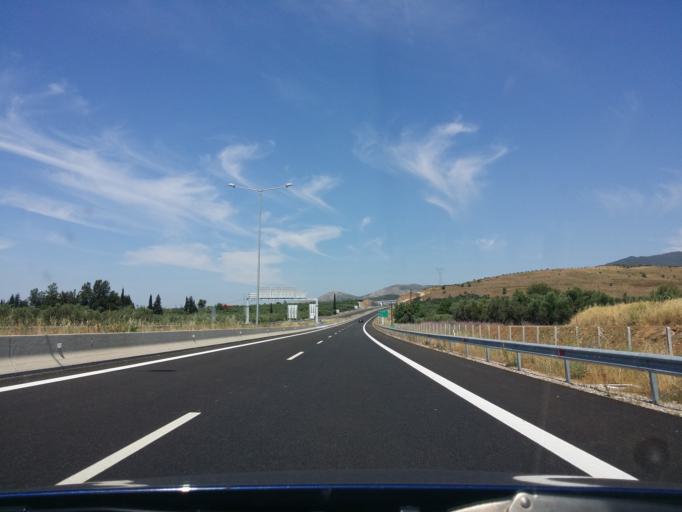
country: GR
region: West Greece
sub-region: Nomos Aitolias kai Akarnanias
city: Mesolongi
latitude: 38.3825
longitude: 21.4923
